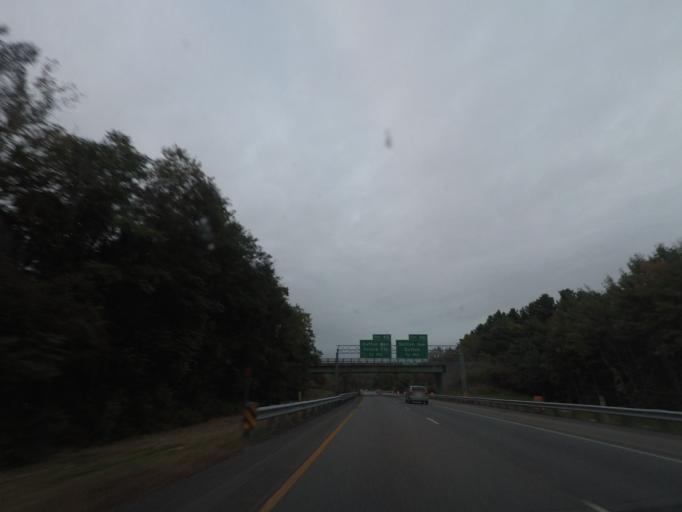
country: US
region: Massachusetts
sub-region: Worcester County
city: Oxford
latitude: 42.1049
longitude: -71.8562
